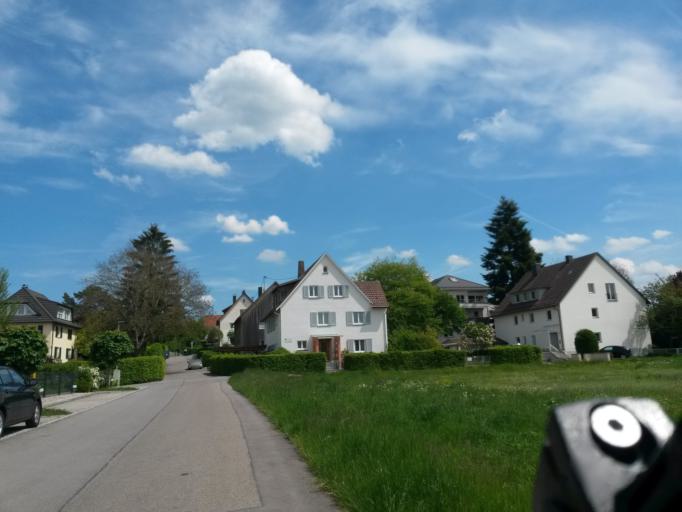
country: DE
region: Baden-Wuerttemberg
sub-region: Tuebingen Region
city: Bad Waldsee
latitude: 47.9198
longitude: 9.7622
